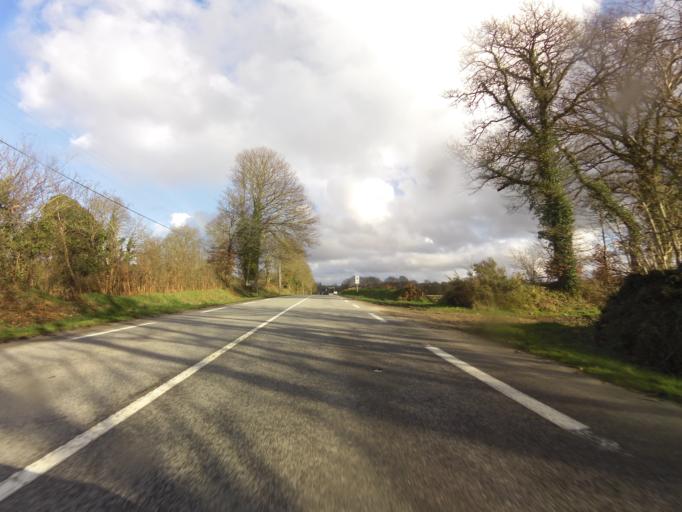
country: FR
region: Brittany
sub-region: Departement du Morbihan
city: Plouray
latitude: 48.1455
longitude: -3.4028
